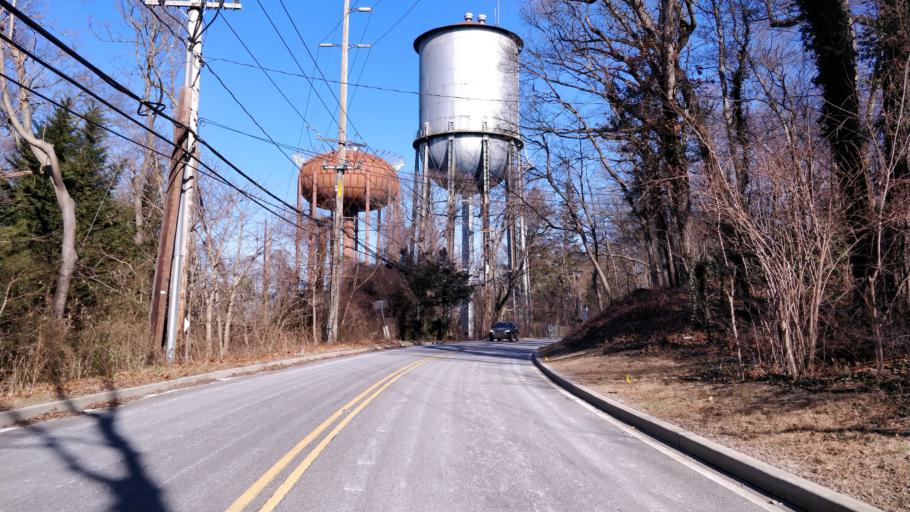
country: US
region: New York
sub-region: Nassau County
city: Brookville
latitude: 40.8117
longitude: -73.5782
